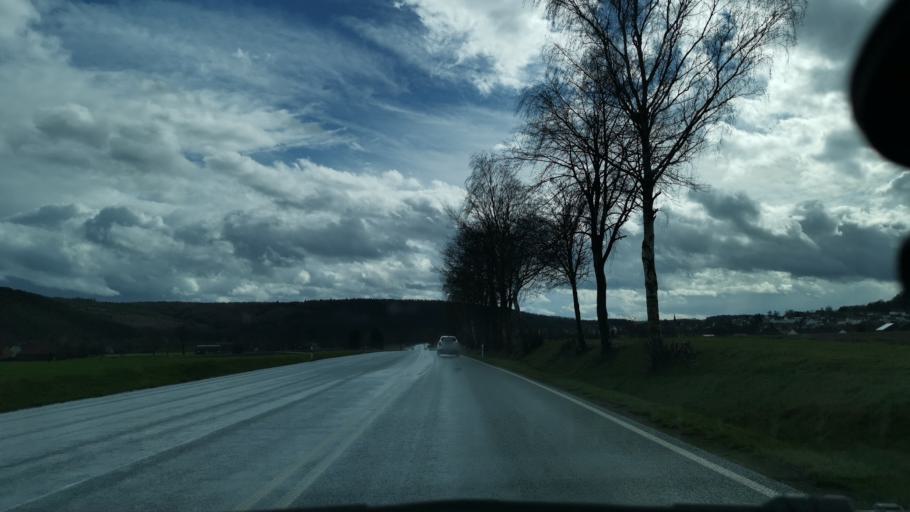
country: DE
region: Hesse
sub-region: Regierungsbezirk Kassel
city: Bad Hersfeld
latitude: 50.9126
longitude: 9.7469
